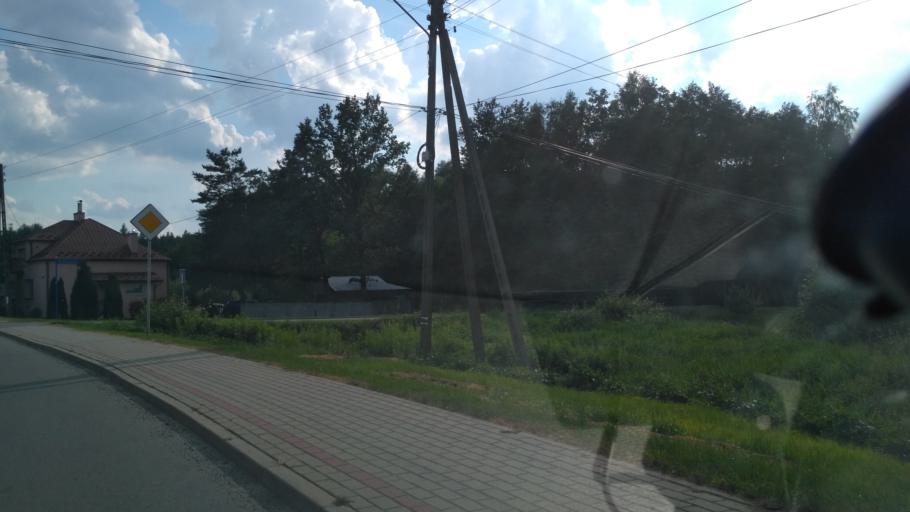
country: PL
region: Subcarpathian Voivodeship
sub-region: Powiat rzeszowski
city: Wysoka Glogowska
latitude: 50.1530
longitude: 22.0178
